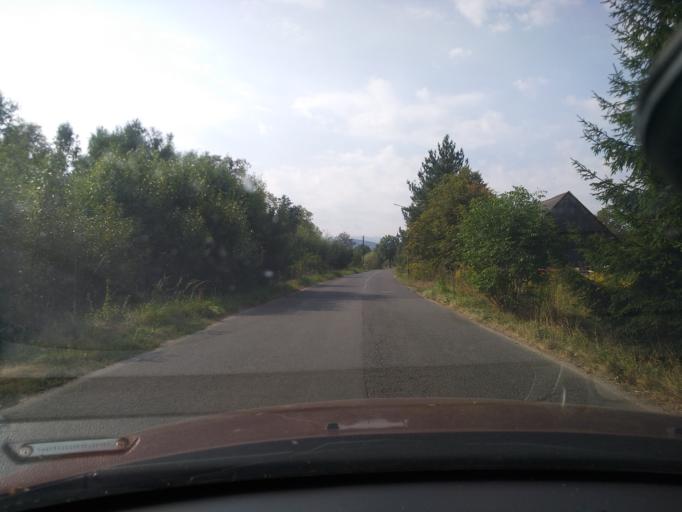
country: PL
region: Lower Silesian Voivodeship
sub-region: Powiat jeleniogorski
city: Stara Kamienica
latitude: 50.9259
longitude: 15.5734
